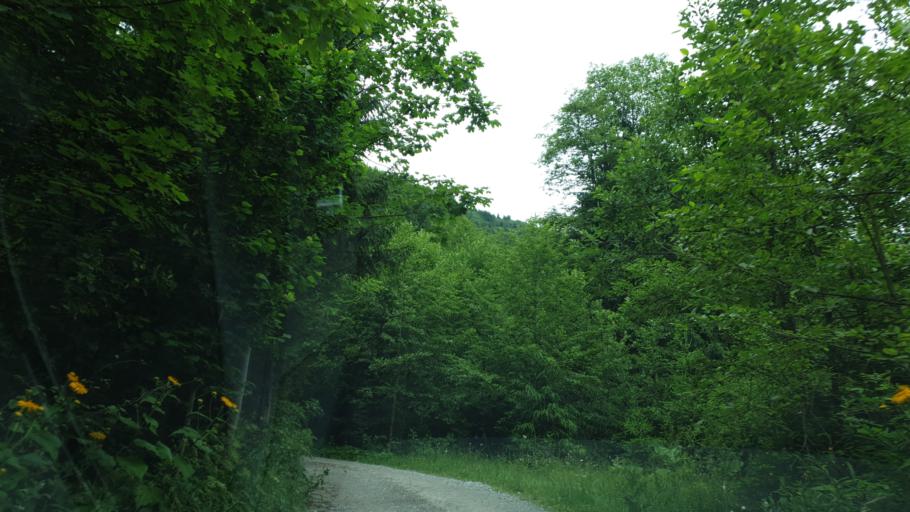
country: RO
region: Hunedoara
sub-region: Comuna Uricani
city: Uricani
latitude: 45.3070
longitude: 22.9860
